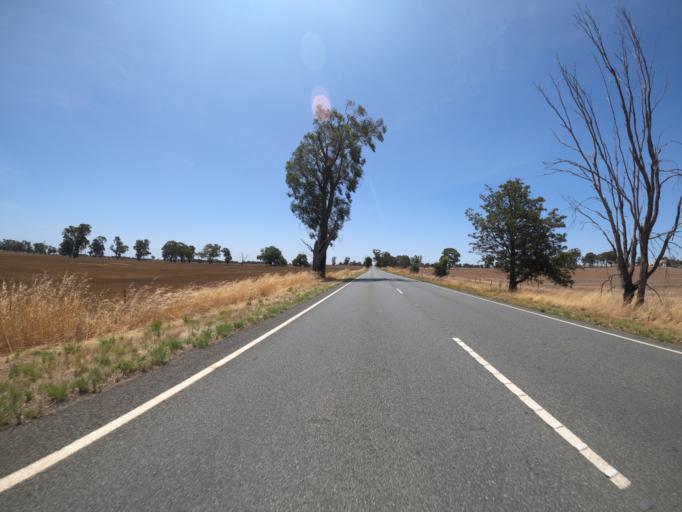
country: AU
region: Victoria
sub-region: Moira
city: Yarrawonga
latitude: -36.0575
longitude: 145.9955
